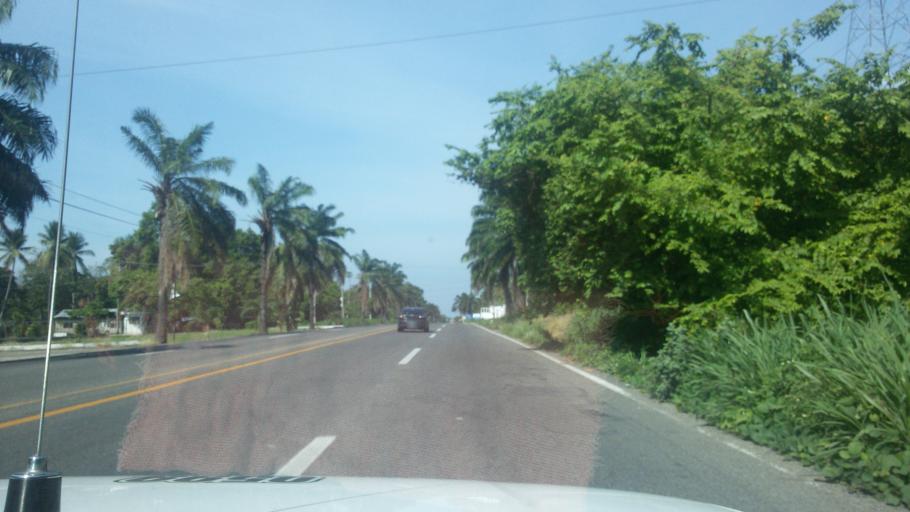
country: MX
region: Chiapas
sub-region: Tapachula
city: Los Cafetales
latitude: 14.8518
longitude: -92.3050
